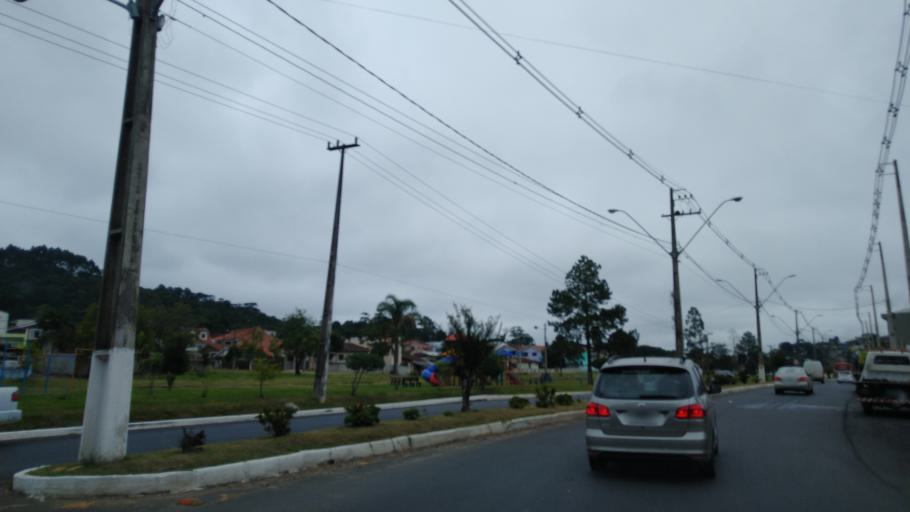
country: BR
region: Santa Catarina
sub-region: Porto Uniao
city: Porto Uniao
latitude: -26.2585
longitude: -51.0724
